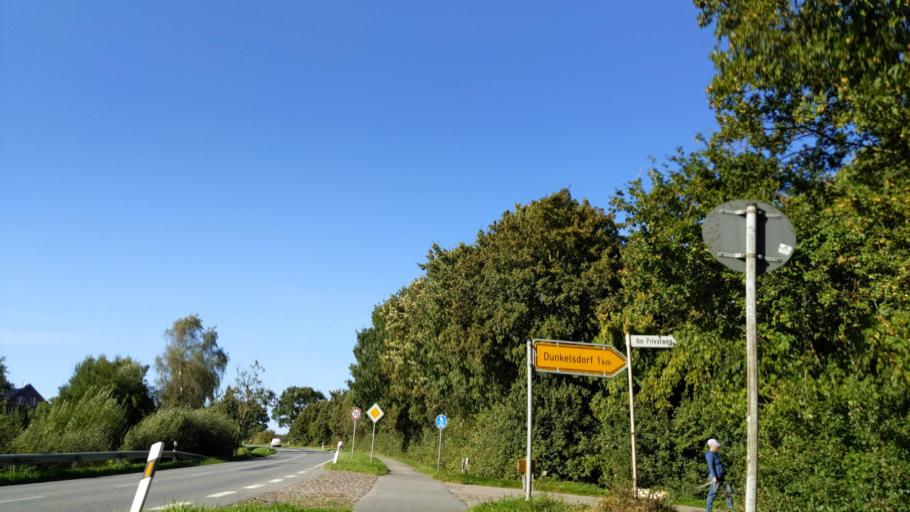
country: DE
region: Schleswig-Holstein
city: Ahrensbok
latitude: 53.9800
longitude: 10.5881
